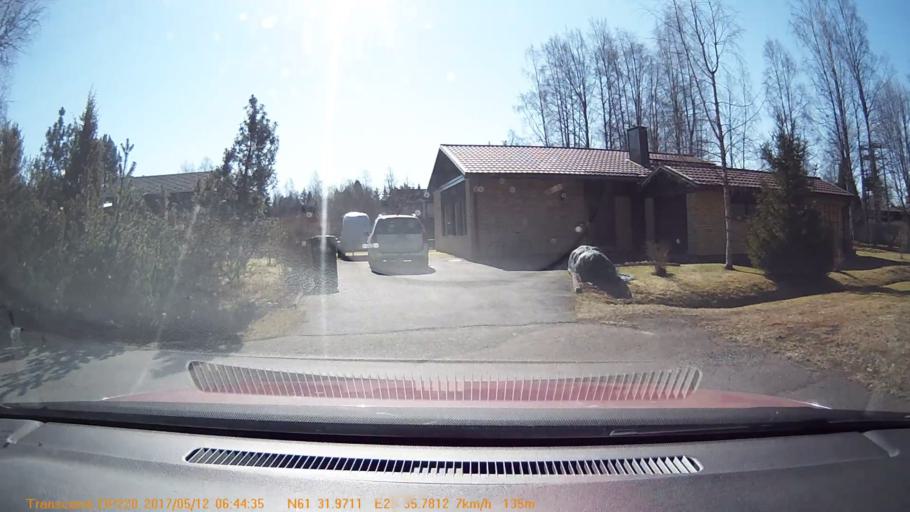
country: FI
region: Pirkanmaa
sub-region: Tampere
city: Yloejaervi
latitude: 61.5329
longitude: 23.5963
